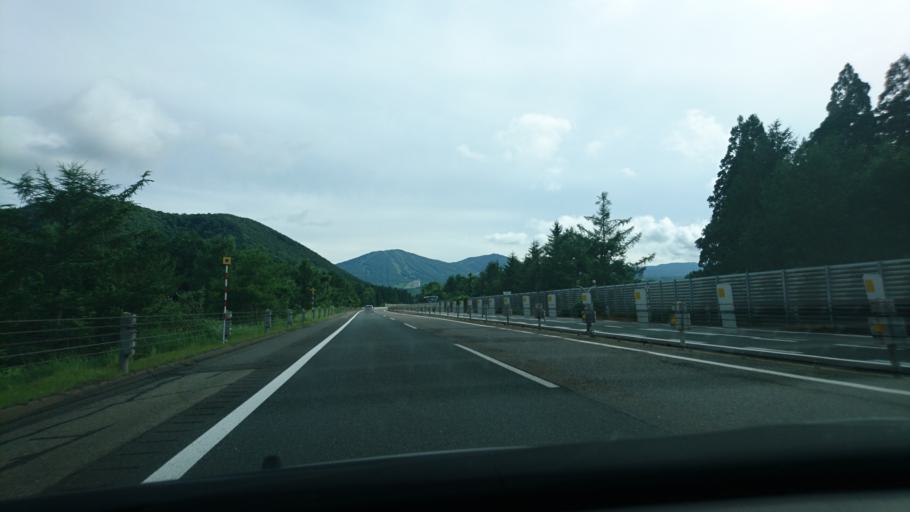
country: JP
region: Akita
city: Hanawa
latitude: 40.0393
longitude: 140.9910
